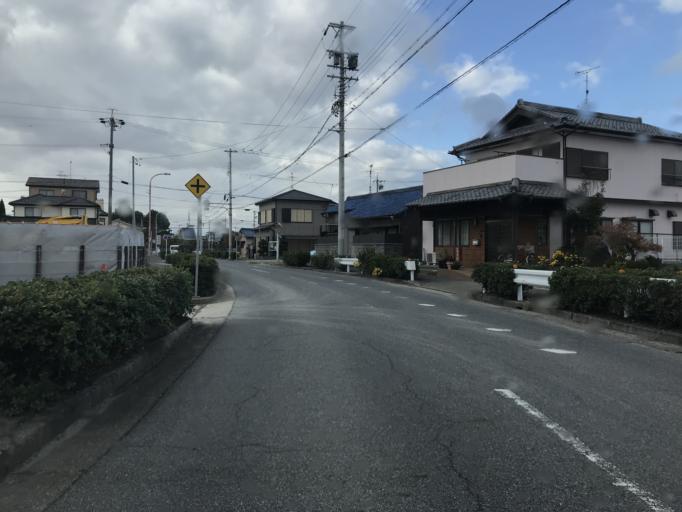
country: JP
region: Aichi
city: Nagoya-shi
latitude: 35.2091
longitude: 136.8422
